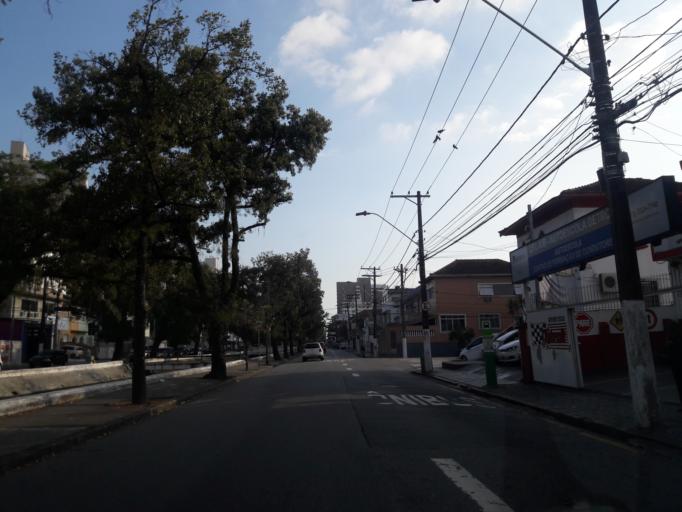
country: BR
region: Sao Paulo
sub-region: Santos
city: Santos
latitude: -23.9507
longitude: -46.3371
